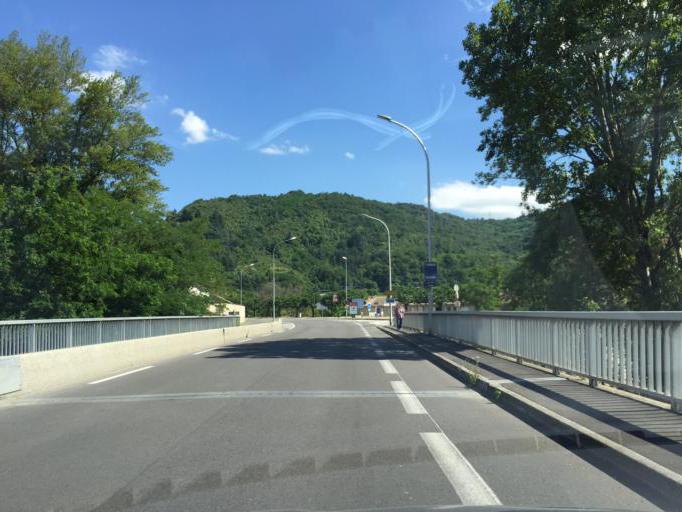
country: FR
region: Rhone-Alpes
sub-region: Departement de l'Ardeche
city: Saint-Jean-de-Muzols
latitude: 45.0745
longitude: 4.8169
